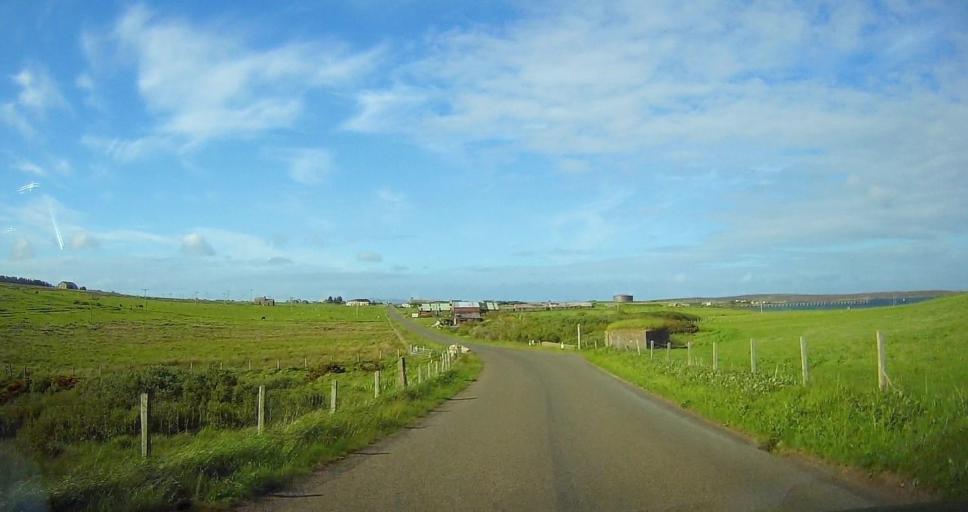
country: GB
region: Scotland
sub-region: Orkney Islands
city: Stromness
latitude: 58.8251
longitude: -3.2101
